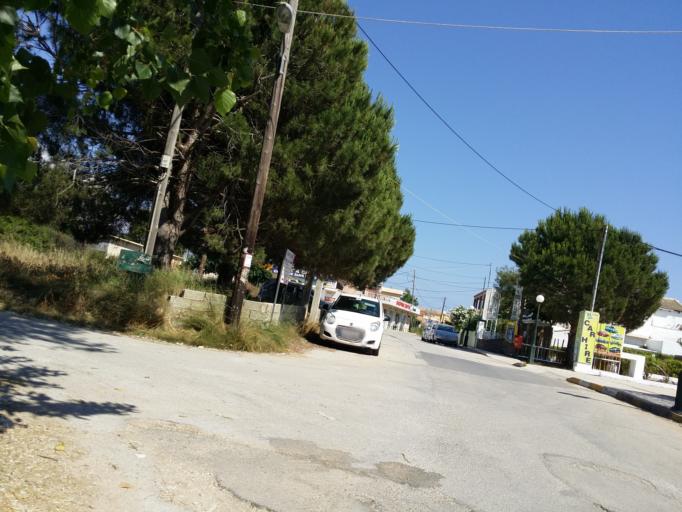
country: GR
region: Ionian Islands
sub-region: Nomos Kerkyras
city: Perivoli
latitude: 39.4279
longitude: 19.9423
